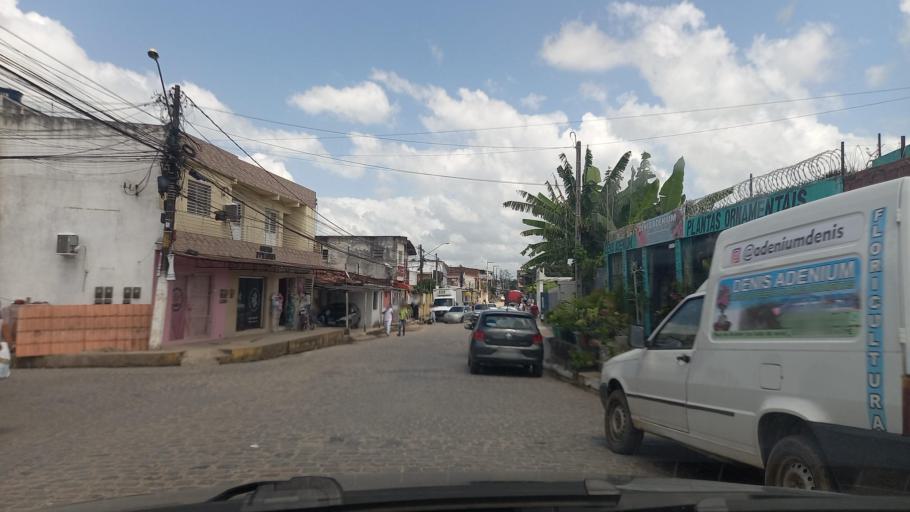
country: BR
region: Pernambuco
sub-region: Goiana
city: Goiana
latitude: -7.5624
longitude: -35.0099
